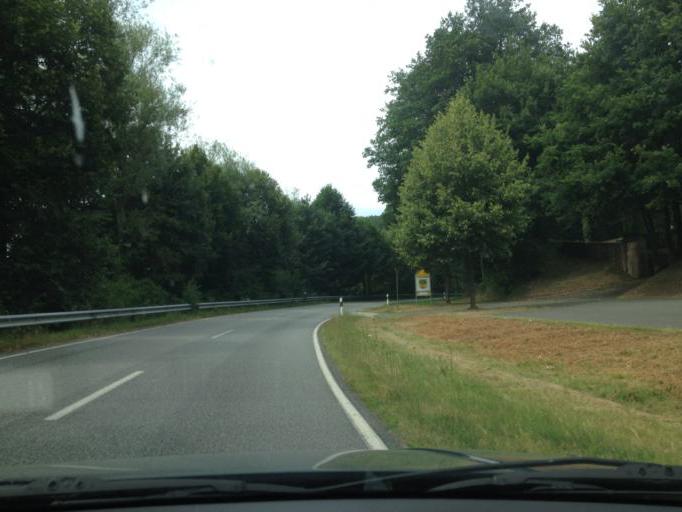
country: DE
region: Rheinland-Pfalz
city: Linden
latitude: 49.3453
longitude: 7.6558
